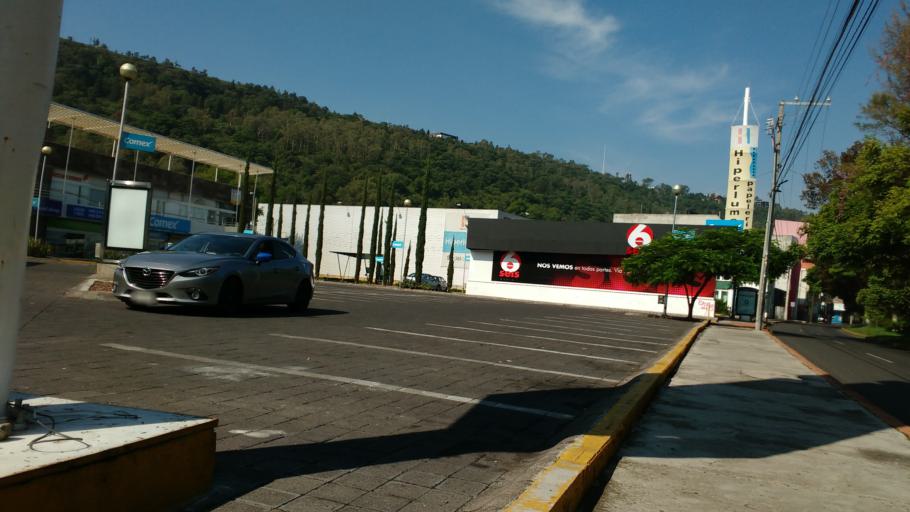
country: MX
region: Michoacan
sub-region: Morelia
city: Montana Monarca (Punta Altozano)
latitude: 19.6830
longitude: -101.1673
